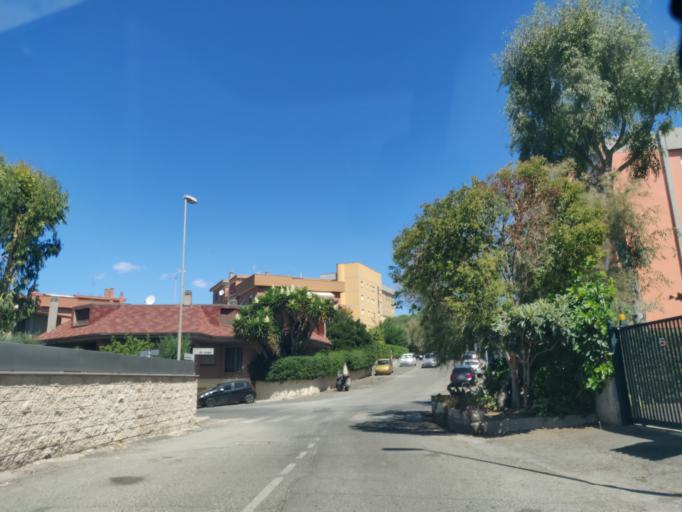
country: IT
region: Latium
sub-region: Citta metropolitana di Roma Capitale
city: Civitavecchia
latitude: 42.0776
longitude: 11.8135
